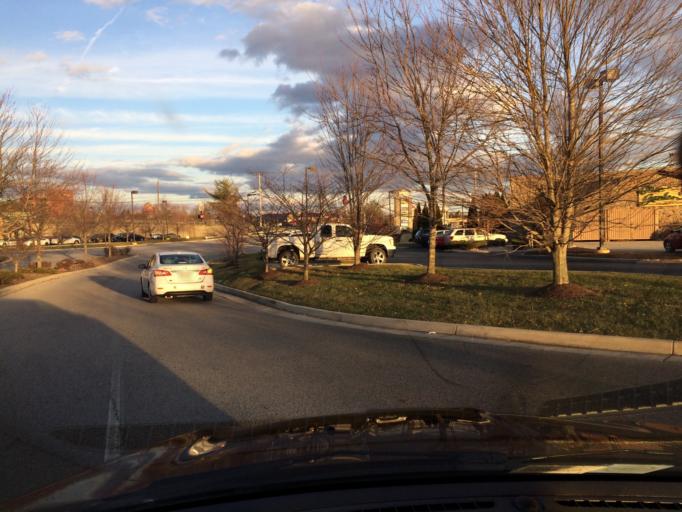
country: US
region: Virginia
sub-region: Montgomery County
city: Merrimac
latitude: 37.1662
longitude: -80.4247
